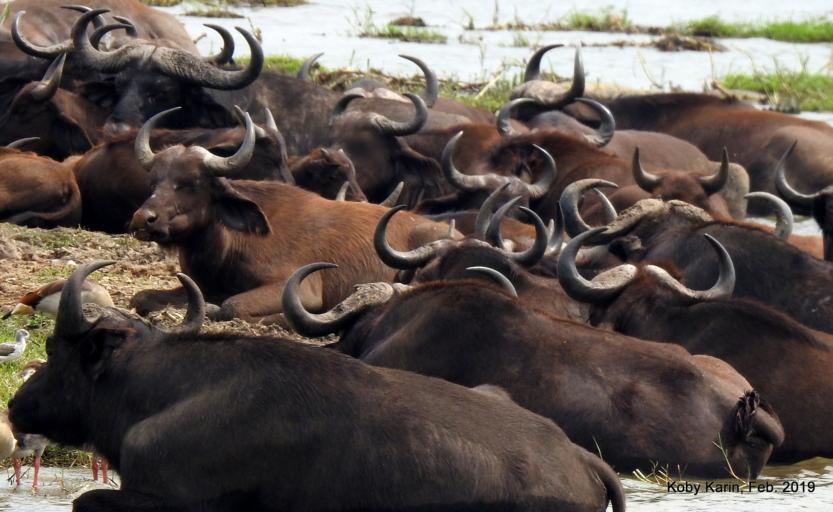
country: UG
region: Western Region
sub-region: Rubirizi District
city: Rubirizi
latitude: -0.1848
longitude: 29.9068
